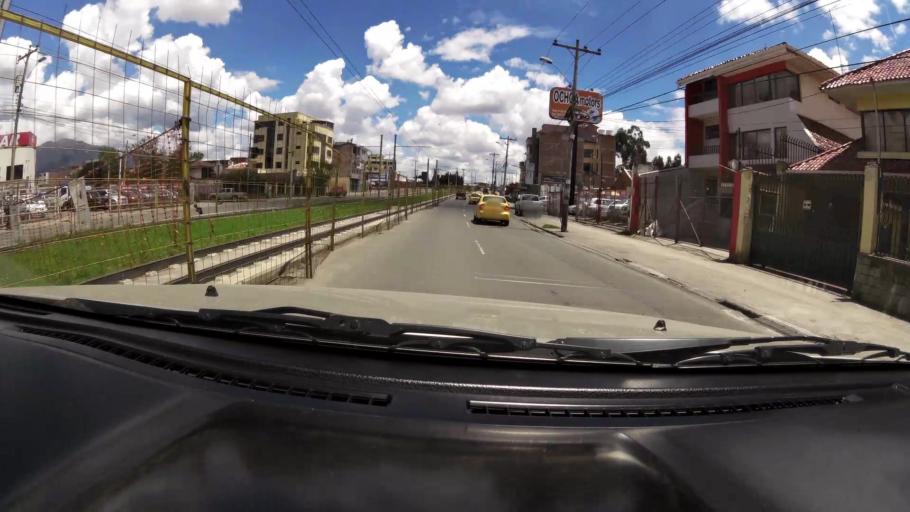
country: EC
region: Azuay
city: Cuenca
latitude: -2.9049
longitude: -79.0322
